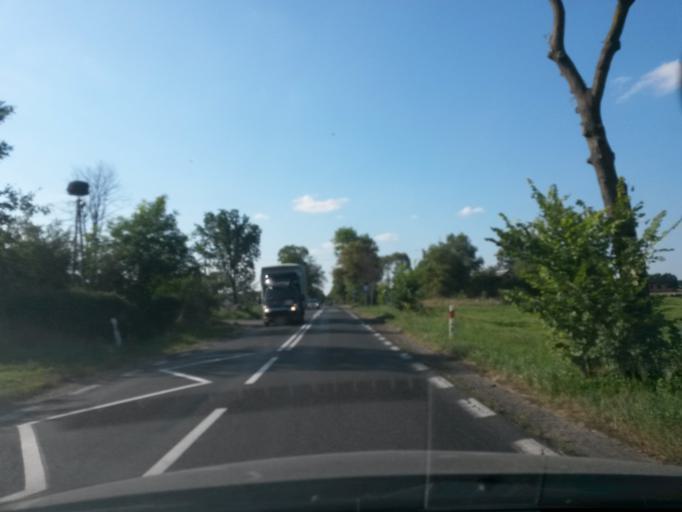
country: PL
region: Masovian Voivodeship
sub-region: Powiat sierpecki
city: Szczutowo
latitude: 52.9119
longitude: 19.6304
